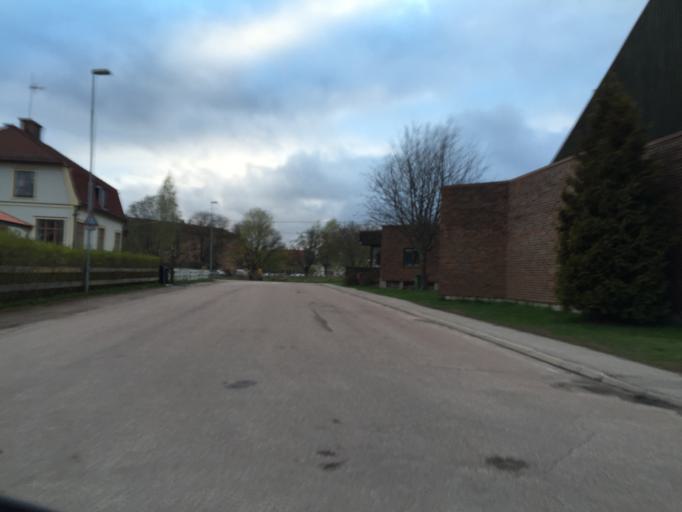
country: SE
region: Dalarna
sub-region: Ludvika Kommun
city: Ludvika
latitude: 60.1460
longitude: 15.1928
